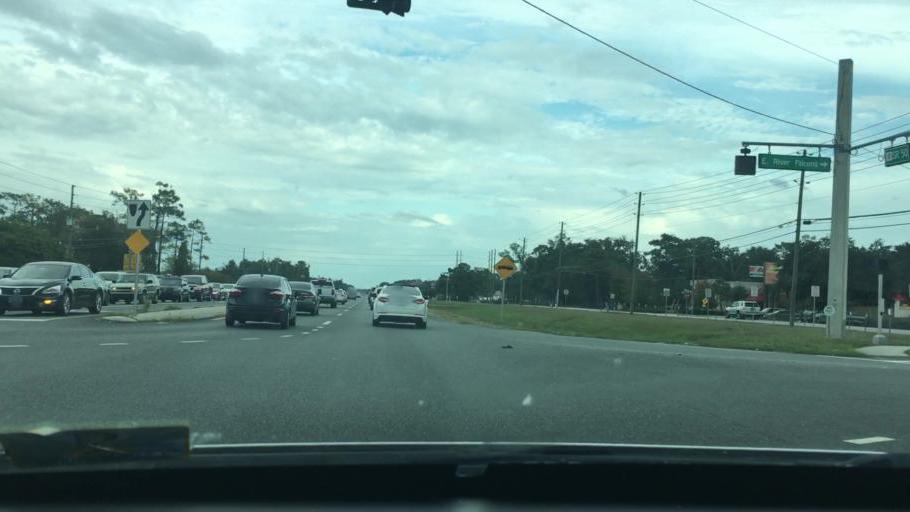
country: US
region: Florida
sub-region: Orange County
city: Bithlo
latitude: 28.5606
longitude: -81.1296
